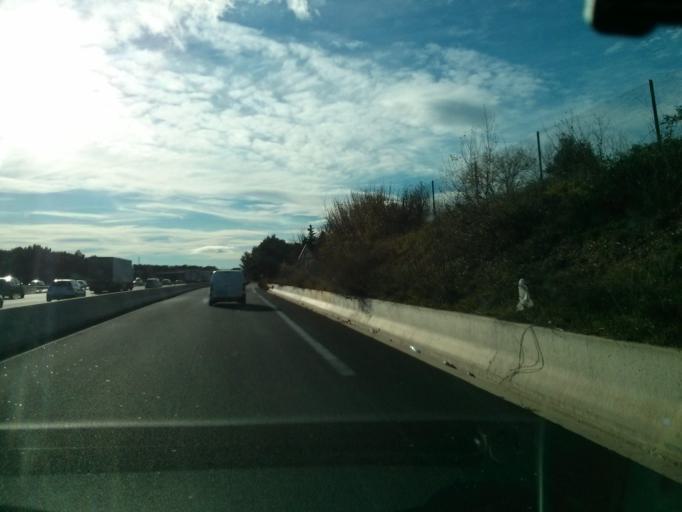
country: FR
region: Languedoc-Roussillon
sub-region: Departement de l'Herault
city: Le Cres
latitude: 43.6090
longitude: 3.9369
